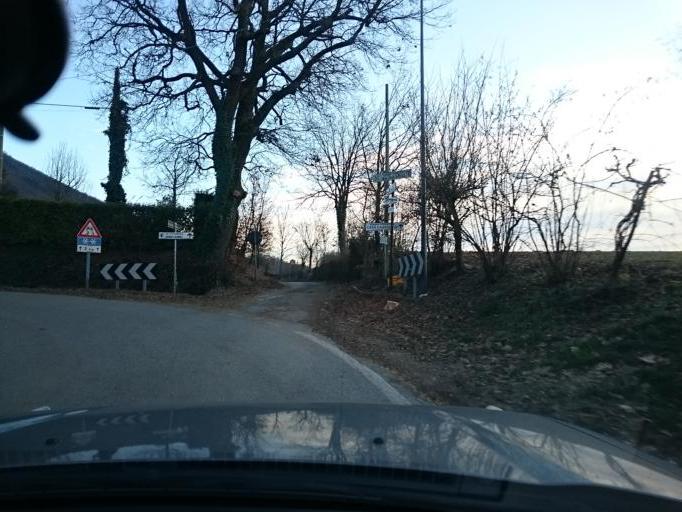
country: IT
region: Veneto
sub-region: Provincia di Padova
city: Vo
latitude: 45.3200
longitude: 11.6542
